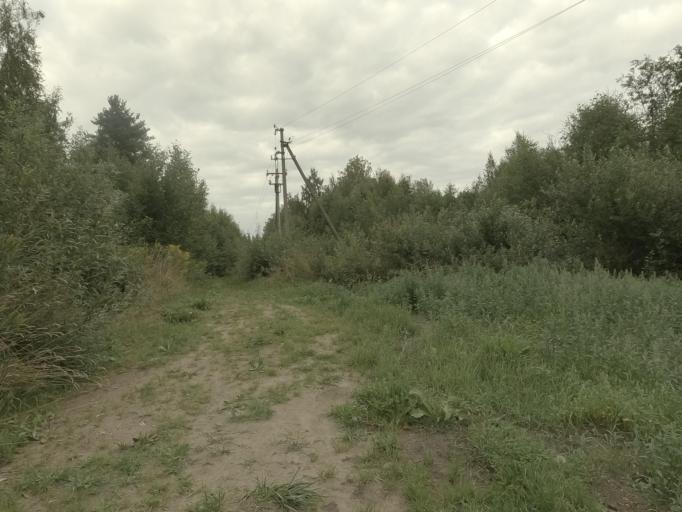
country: RU
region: Leningrad
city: Kirovsk
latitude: 59.9049
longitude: 31.0022
